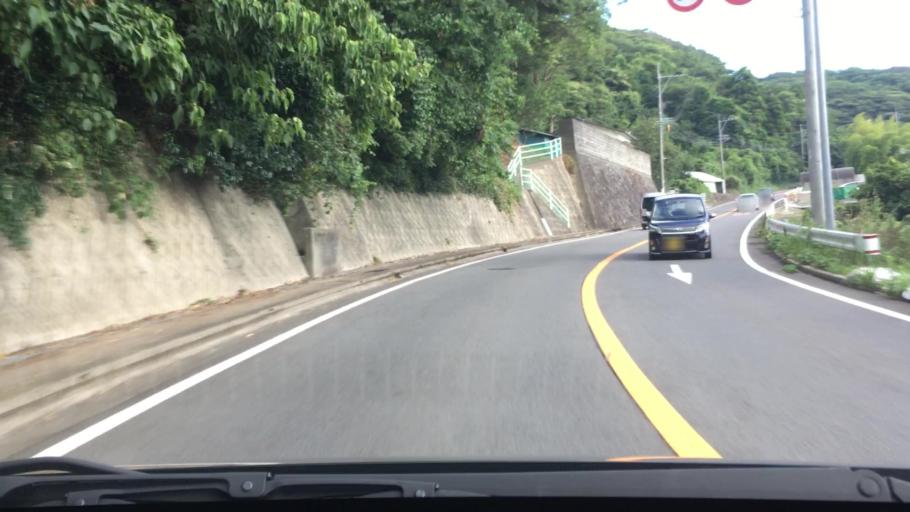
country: JP
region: Nagasaki
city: Togitsu
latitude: 32.8283
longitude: 129.7251
